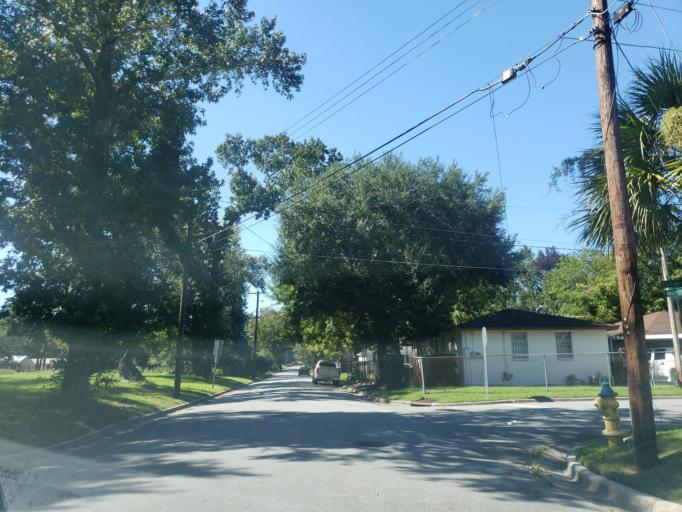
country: US
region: Georgia
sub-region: Chatham County
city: Savannah
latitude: 32.0498
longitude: -81.1121
